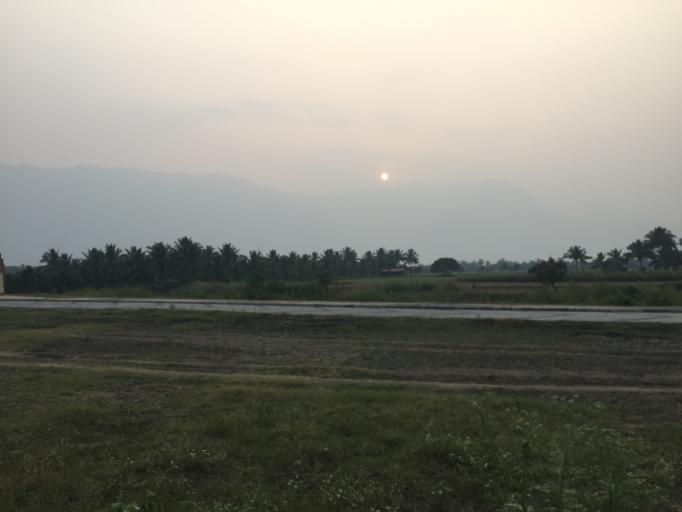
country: IN
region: Tamil Nadu
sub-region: Coimbatore
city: Perur
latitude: 10.9636
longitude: 76.7423
